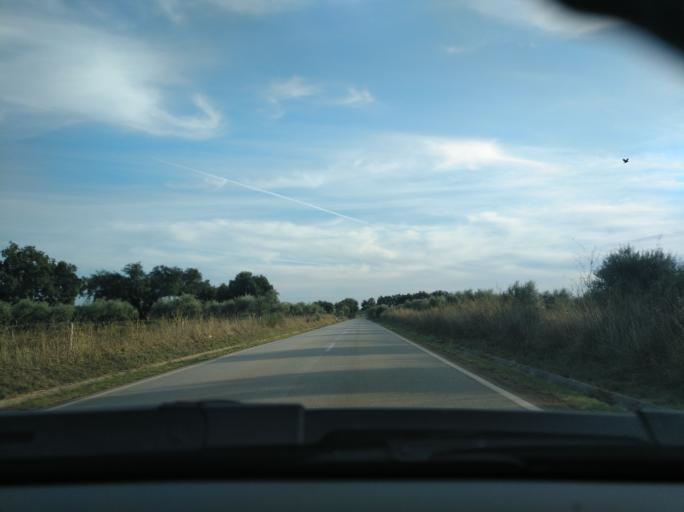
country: PT
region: Portalegre
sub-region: Avis
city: Avis
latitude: 38.9282
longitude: -7.8102
